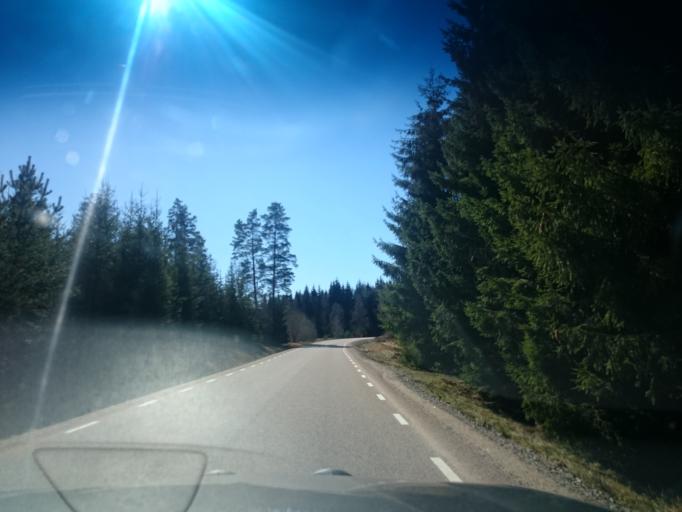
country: SE
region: Joenkoeping
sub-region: Vetlanda Kommun
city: Landsbro
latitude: 57.2281
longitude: 14.9921
